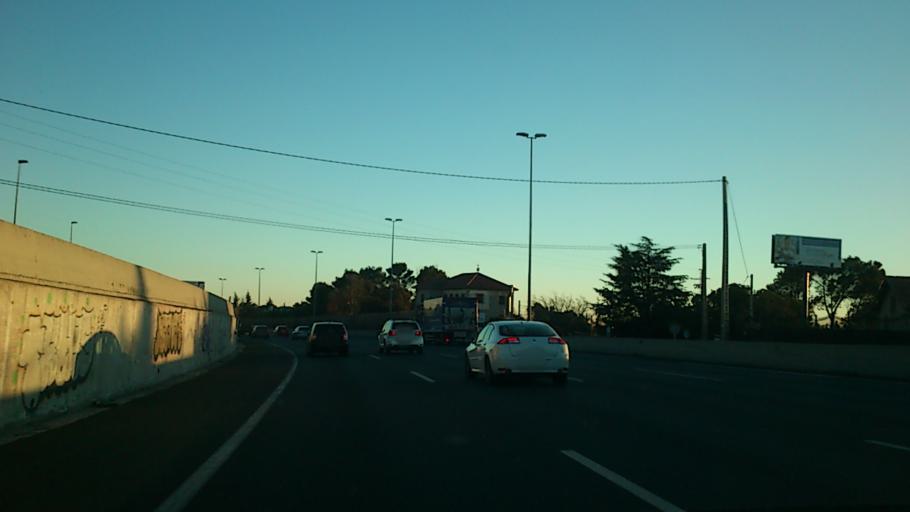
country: ES
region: Madrid
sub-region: Provincia de Madrid
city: Torrelodones
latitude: 40.5878
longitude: -3.9542
